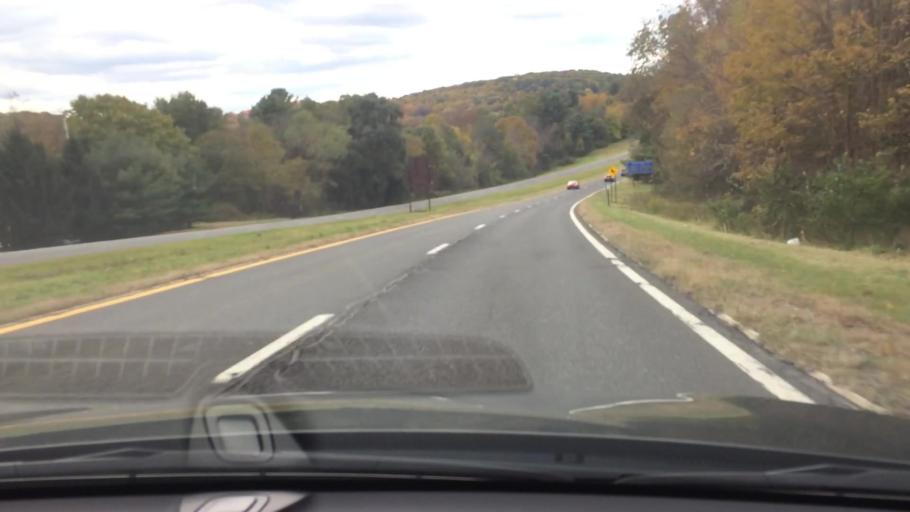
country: US
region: New York
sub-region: Dutchess County
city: Hillside Lake
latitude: 41.6765
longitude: -73.7874
